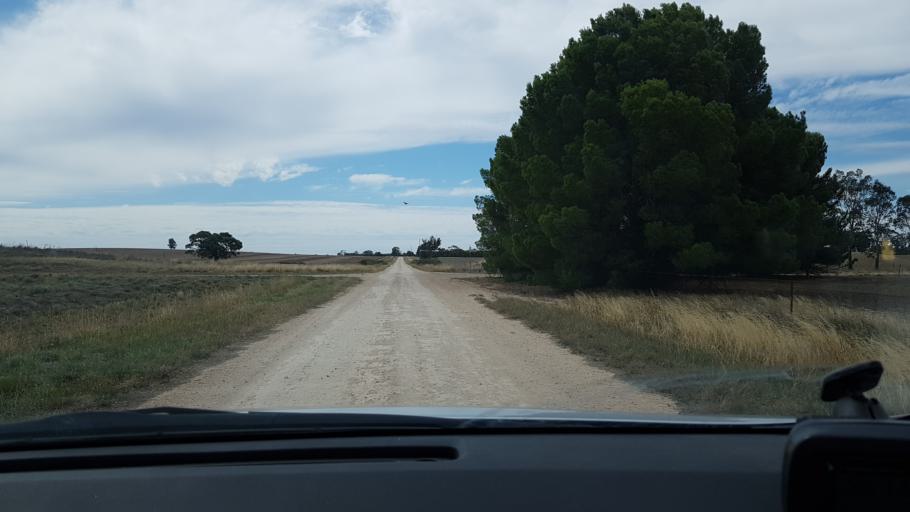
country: AU
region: Victoria
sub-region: Horsham
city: Horsham
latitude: -36.7053
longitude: 141.7806
